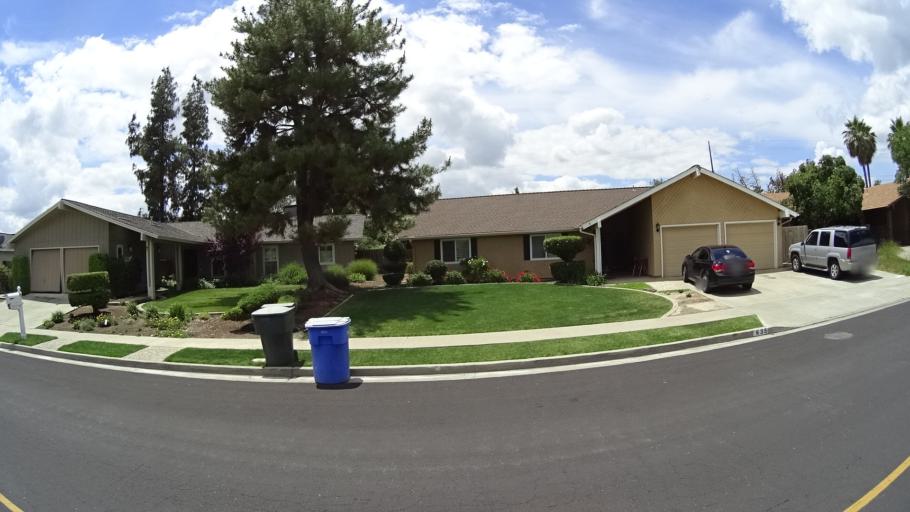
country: US
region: California
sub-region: Kings County
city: Lucerne
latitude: 36.3545
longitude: -119.6540
